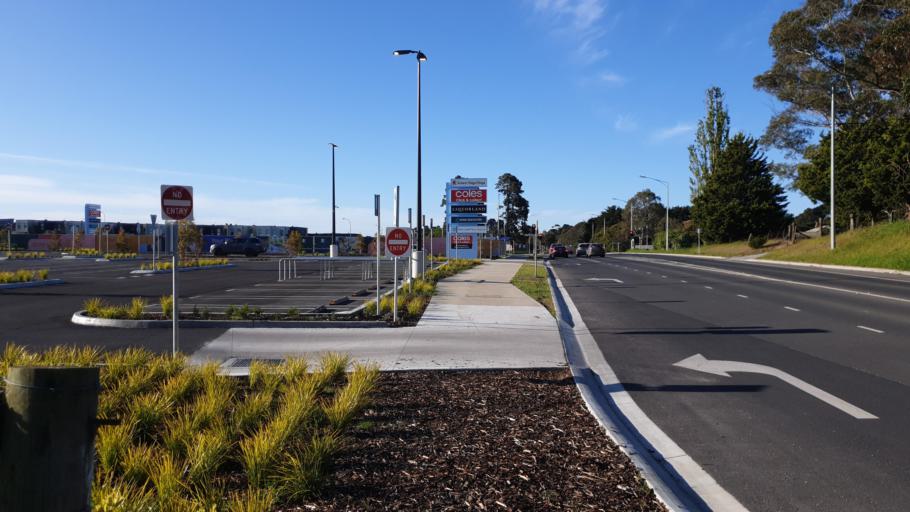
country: AU
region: Victoria
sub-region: Casey
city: Junction Village
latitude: -38.1504
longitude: 145.2915
